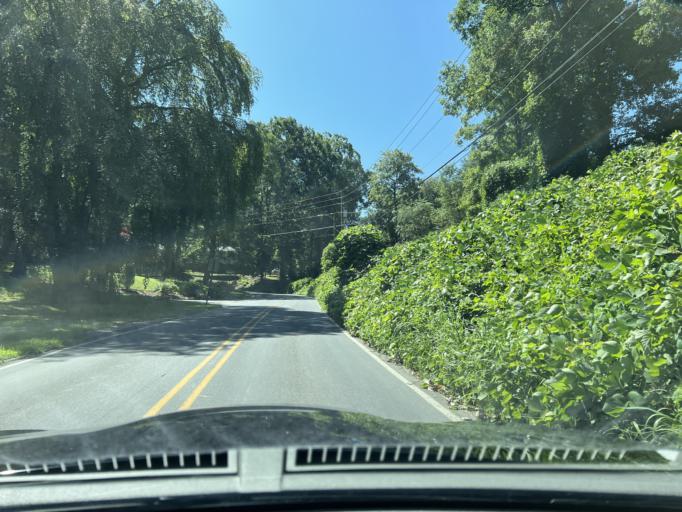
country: US
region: North Carolina
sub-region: Buncombe County
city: Biltmore Forest
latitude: 35.5709
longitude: -82.5152
